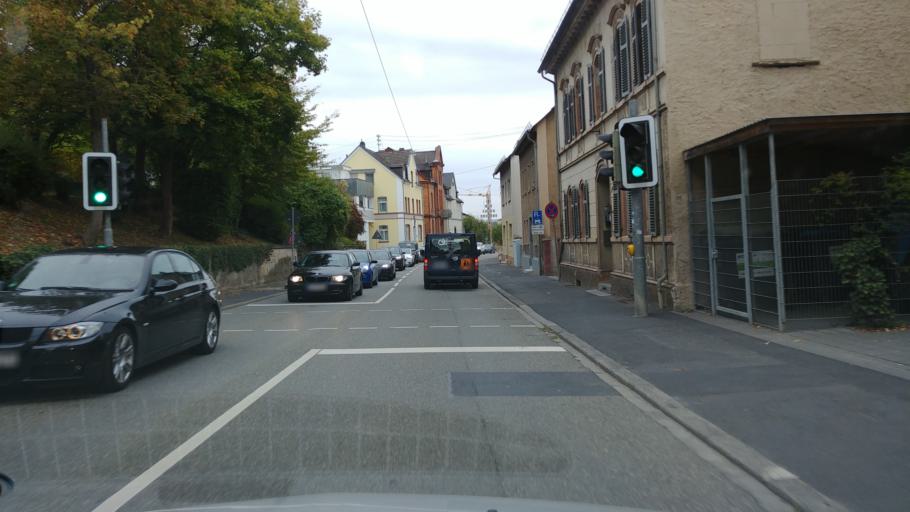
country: DE
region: Rheinland-Pfalz
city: Hahnstatten
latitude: 50.3067
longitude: 8.0667
